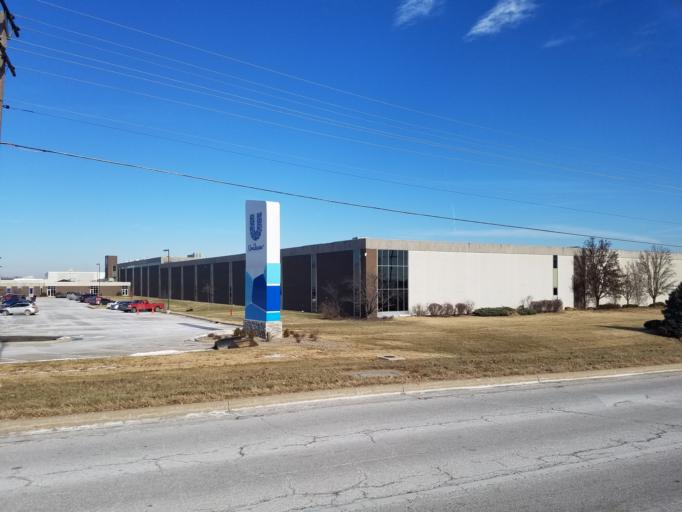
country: US
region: Missouri
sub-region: Cole County
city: Jefferson City
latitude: 38.5914
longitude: -92.2445
